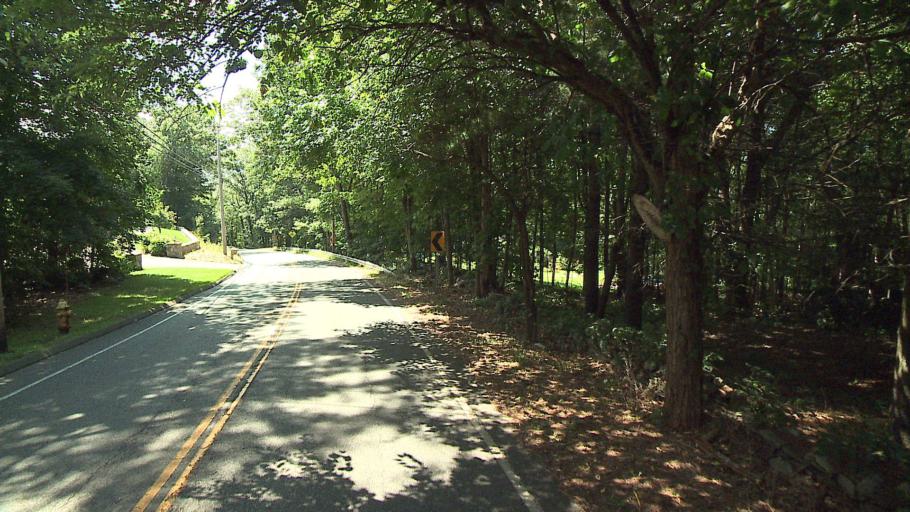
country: US
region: Connecticut
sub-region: Fairfield County
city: Shelton
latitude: 41.3010
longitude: -73.1374
